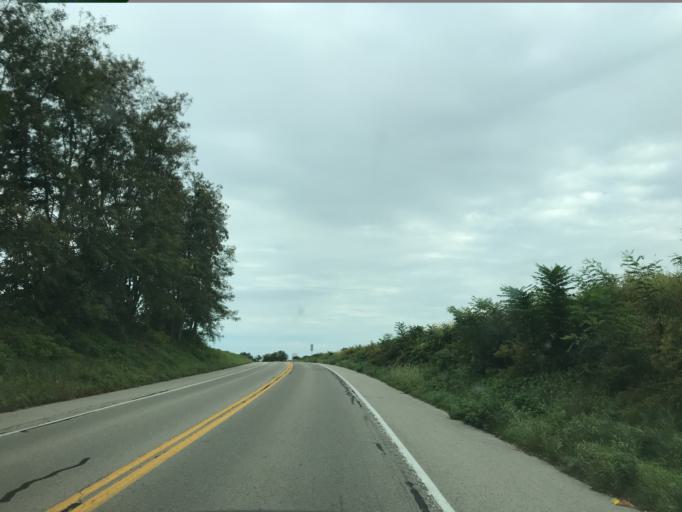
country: US
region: Pennsylvania
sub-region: Erie County
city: North East
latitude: 42.2380
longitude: -79.7695
